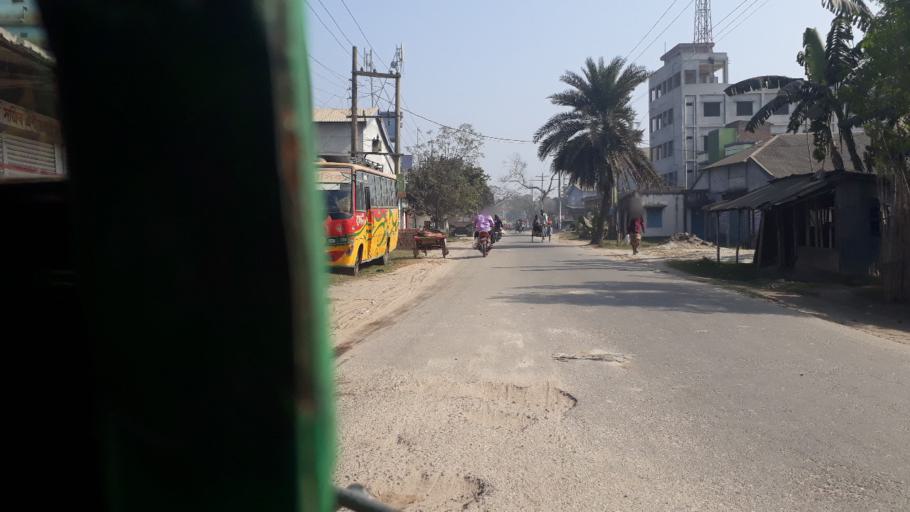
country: BD
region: Khulna
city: Kushtia
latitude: 23.8614
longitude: 89.0411
